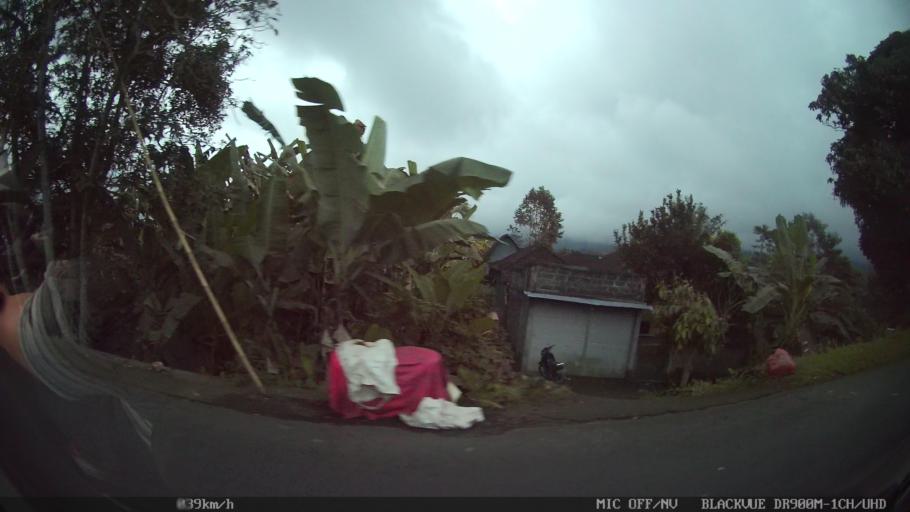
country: ID
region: Bali
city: Peneng
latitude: -8.3504
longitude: 115.1840
